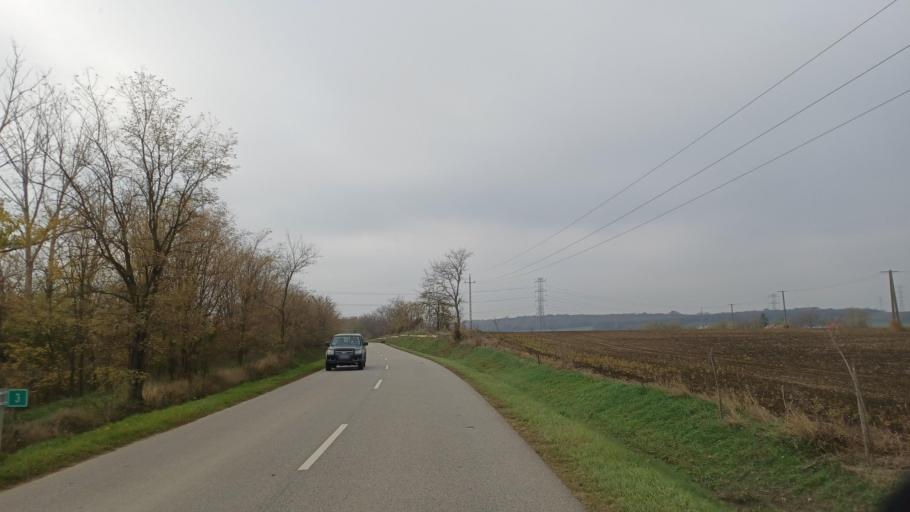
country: HU
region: Tolna
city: Dunaszentgyorgy
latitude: 46.5831
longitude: 18.7923
